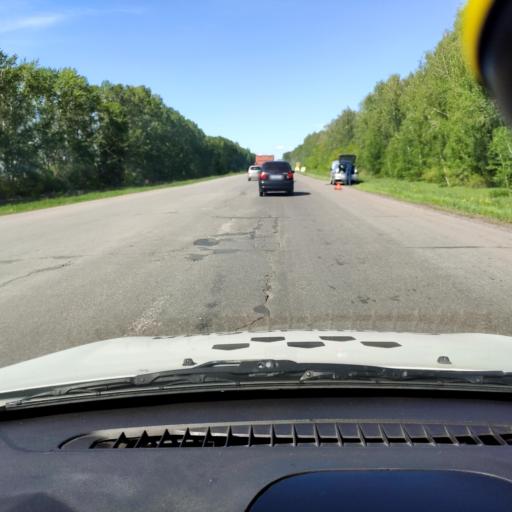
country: RU
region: Samara
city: Tol'yatti
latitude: 53.6401
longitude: 49.4200
